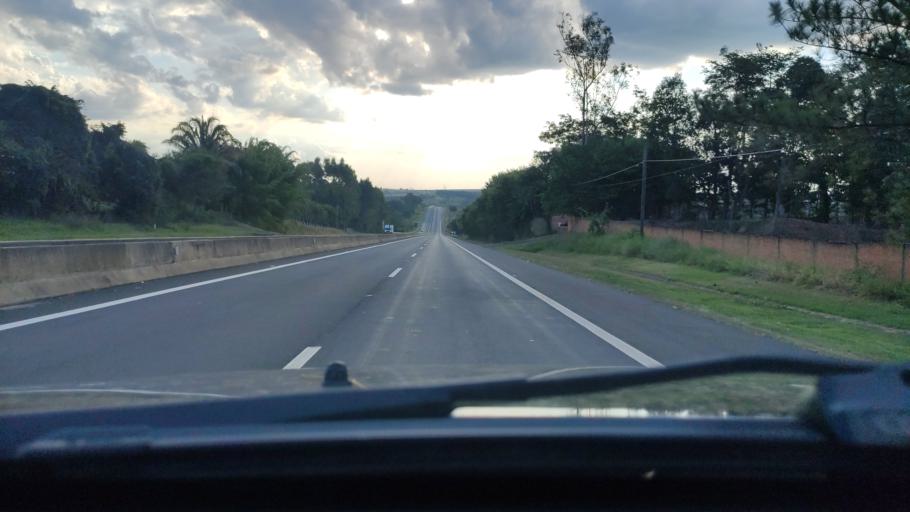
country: BR
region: Sao Paulo
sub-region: Mogi-Mirim
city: Mogi Mirim
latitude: -22.4435
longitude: -47.0353
